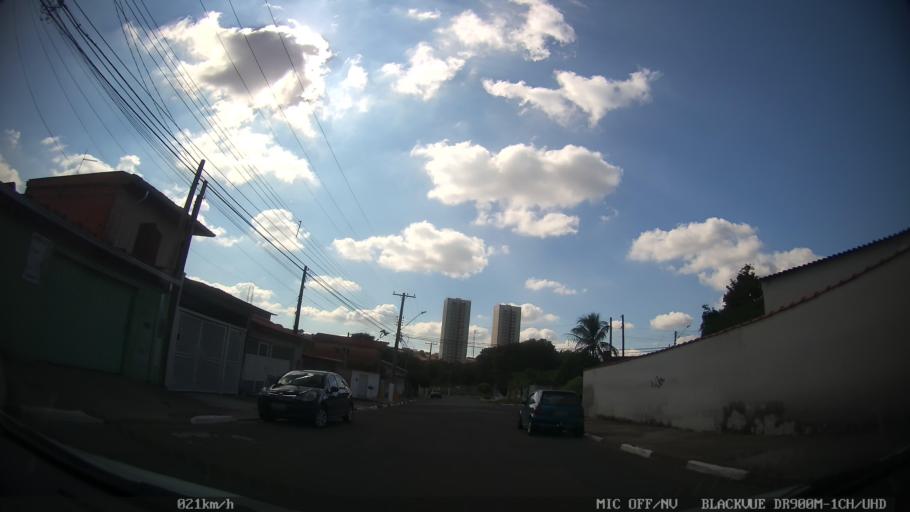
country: BR
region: Sao Paulo
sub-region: Hortolandia
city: Hortolandia
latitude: -22.8909
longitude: -47.2014
